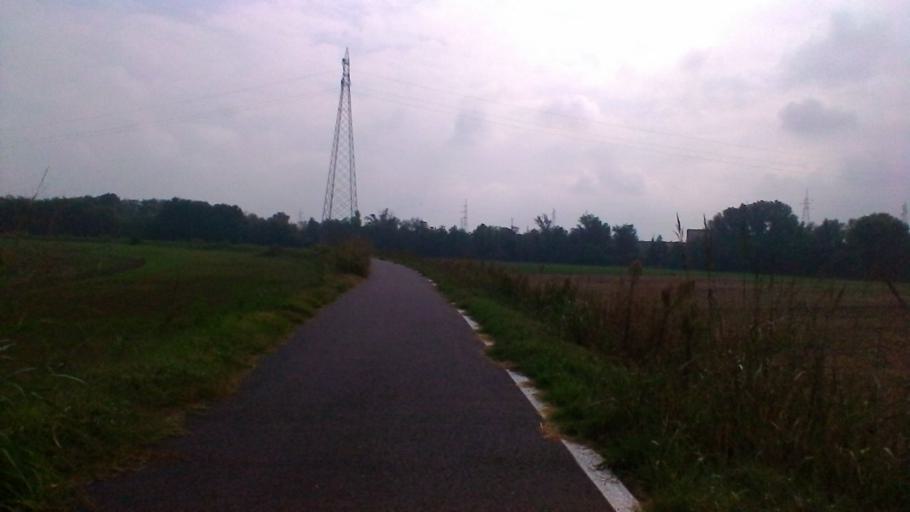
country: IT
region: Veneto
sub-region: Provincia di Verona
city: San Giovanni Lupatoto
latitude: 45.3964
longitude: 11.0341
